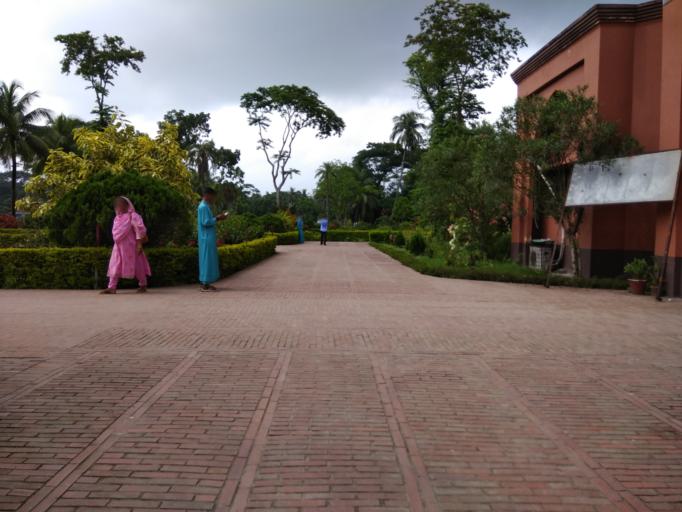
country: BD
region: Khulna
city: Khulna
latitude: 22.6735
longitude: 89.7426
